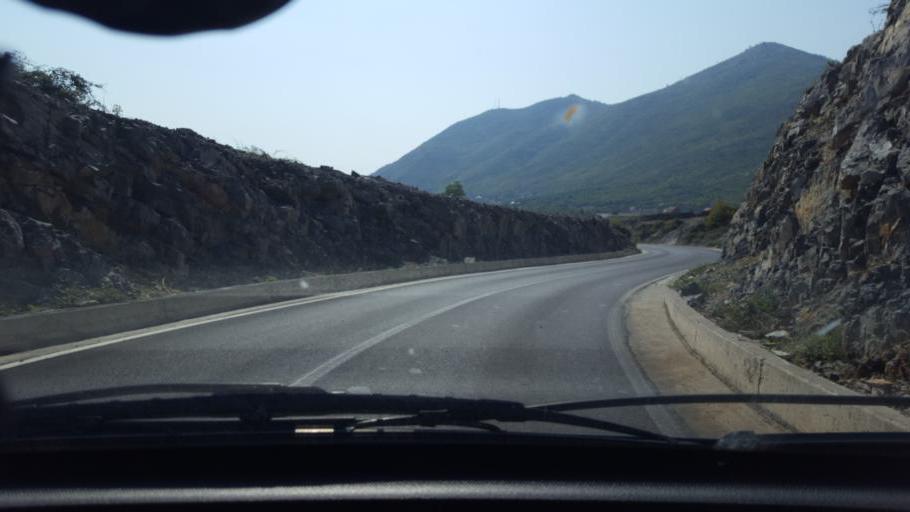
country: AL
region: Shkoder
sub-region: Rrethi i Malesia e Madhe
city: Kastrat
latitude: 42.4099
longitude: 19.5041
